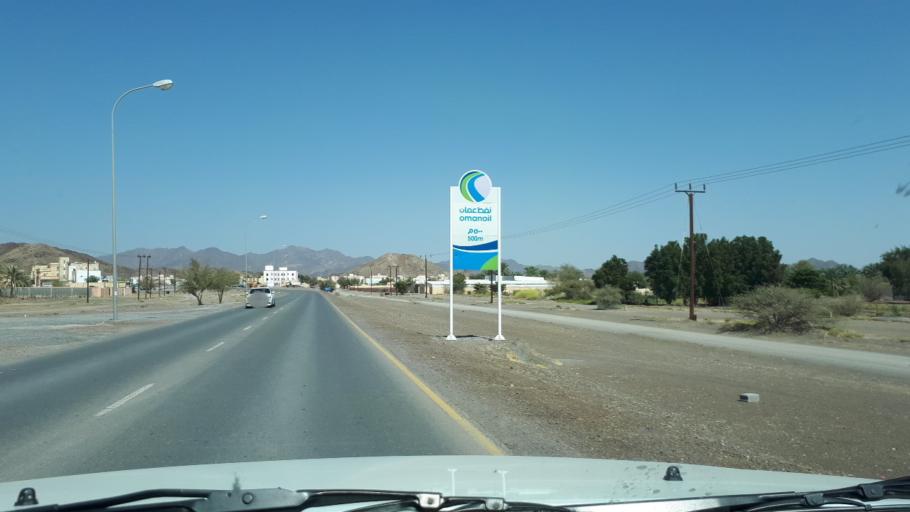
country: OM
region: Muhafazat ad Dakhiliyah
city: Bahla'
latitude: 22.9474
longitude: 57.2788
